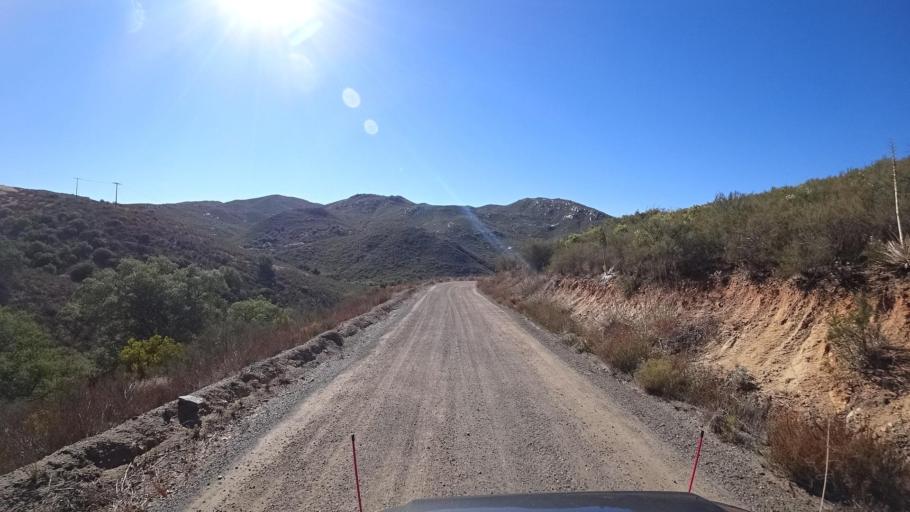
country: US
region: California
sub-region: San Diego County
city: Descanso
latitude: 32.8656
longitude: -116.6592
